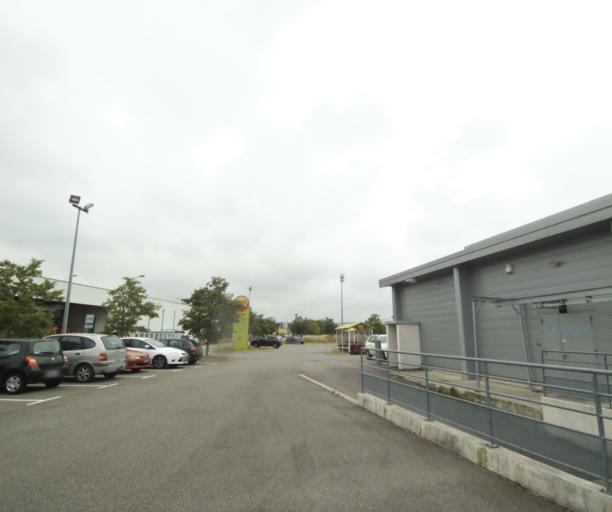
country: FR
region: Midi-Pyrenees
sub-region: Departement du Tarn-et-Garonne
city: Bressols
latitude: 43.9863
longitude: 1.3318
